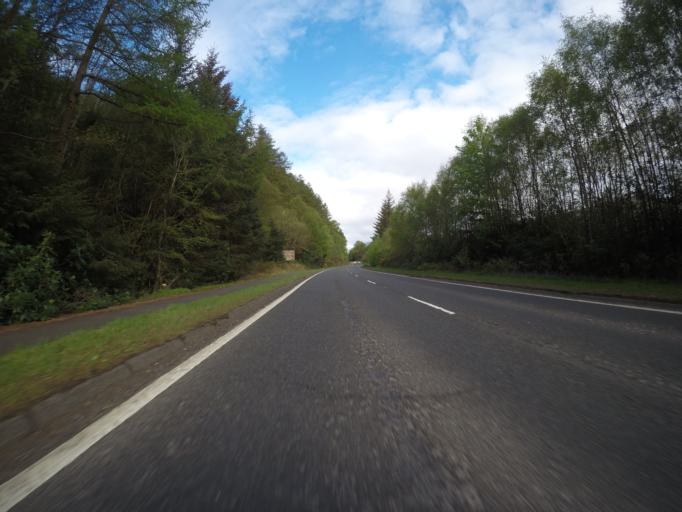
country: GB
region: Scotland
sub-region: Highland
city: Fort William
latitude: 56.6819
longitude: -5.1653
